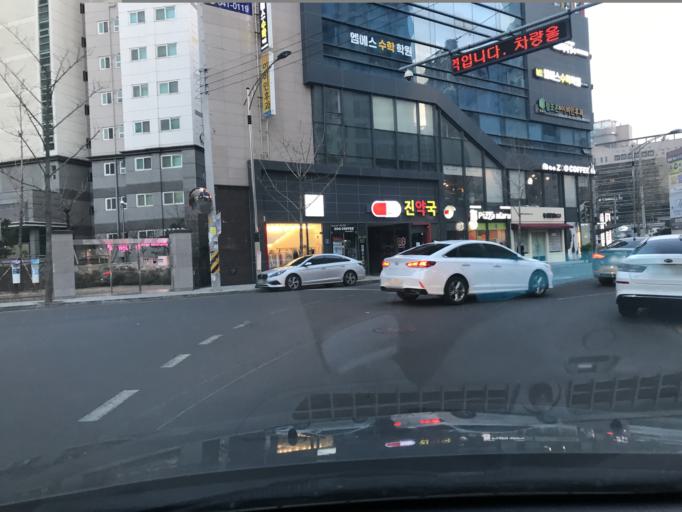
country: KR
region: Daegu
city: Hwawon
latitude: 35.8151
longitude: 128.5205
